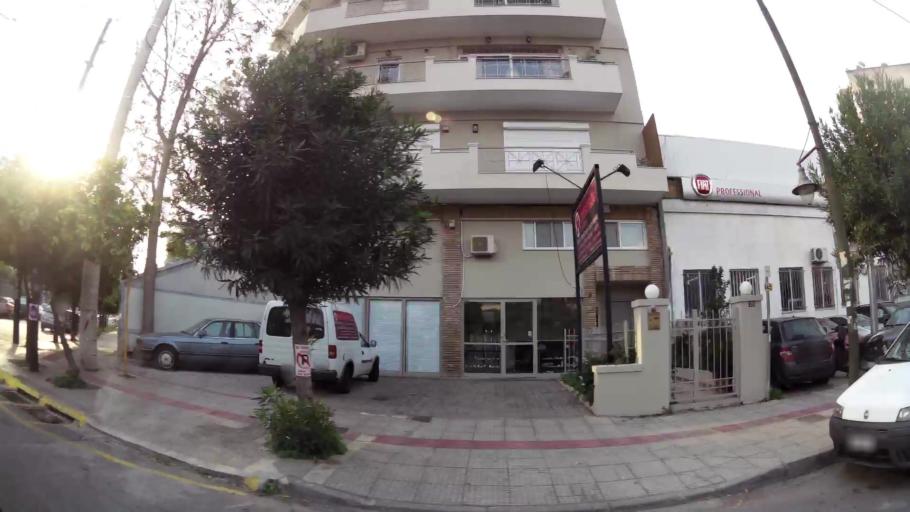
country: GR
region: Attica
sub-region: Nomarchia Athinas
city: Kallithea
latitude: 37.9444
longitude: 23.6961
